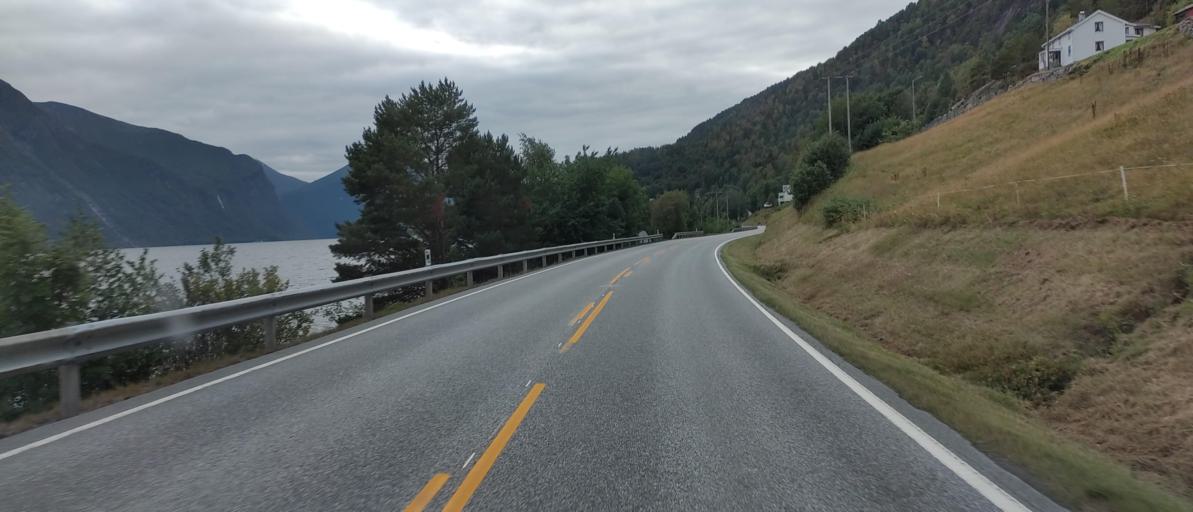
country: NO
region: More og Romsdal
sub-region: Rauma
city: Andalsnes
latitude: 62.5773
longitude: 7.6728
